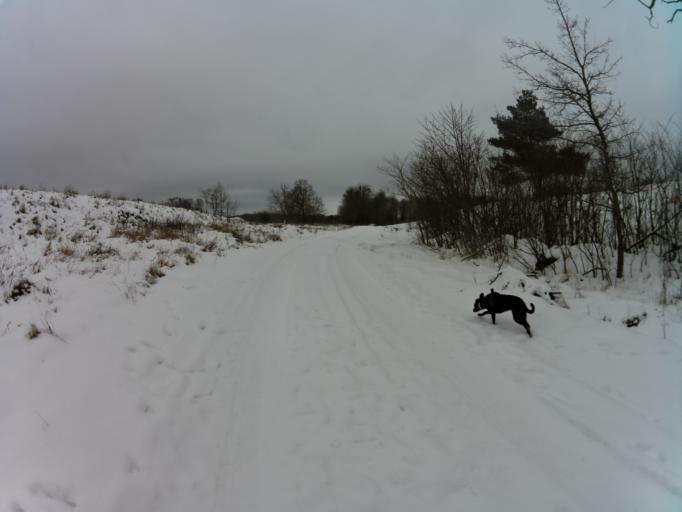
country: PL
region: West Pomeranian Voivodeship
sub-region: Powiat choszczenski
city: Recz
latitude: 53.3392
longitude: 15.5401
